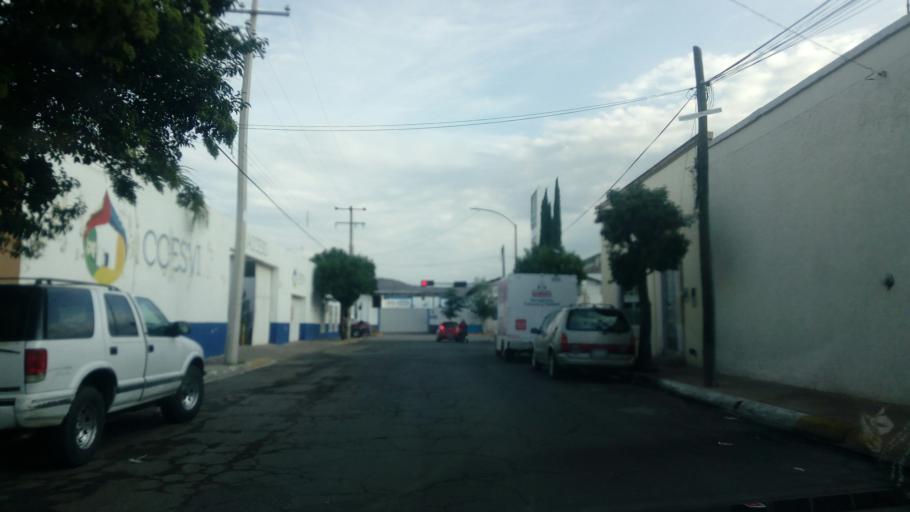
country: MX
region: Durango
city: Victoria de Durango
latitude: 24.0343
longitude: -104.6676
